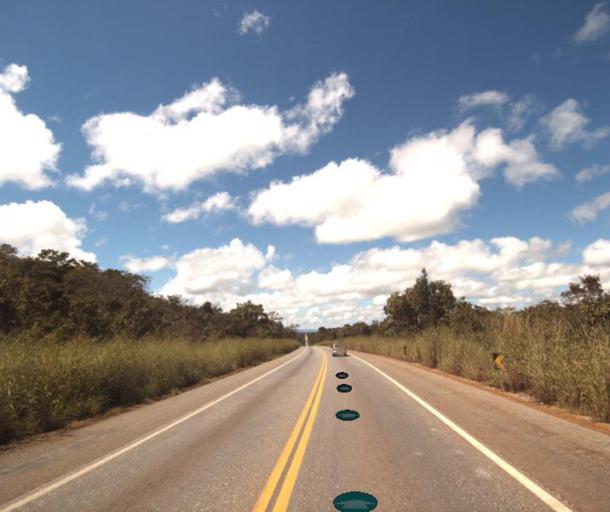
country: BR
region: Goias
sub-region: Jaragua
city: Jaragua
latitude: -15.8999
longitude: -49.2333
